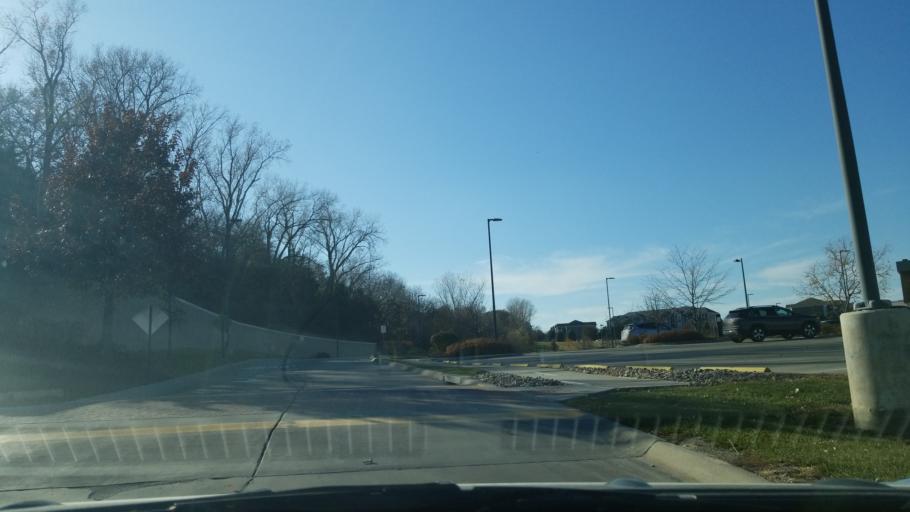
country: US
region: Nebraska
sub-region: Sarpy County
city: Offutt Air Force Base
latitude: 41.1364
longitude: -95.9455
